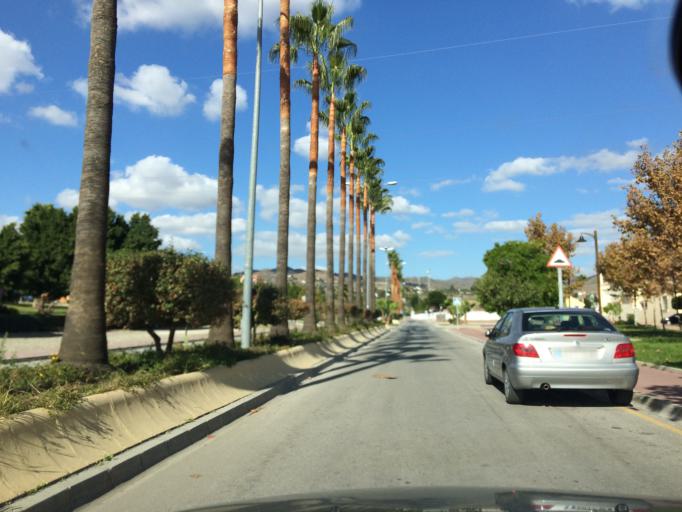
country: ES
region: Andalusia
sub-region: Provincia de Malaga
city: Estacion de Cartama
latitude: 36.7377
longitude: -4.6143
